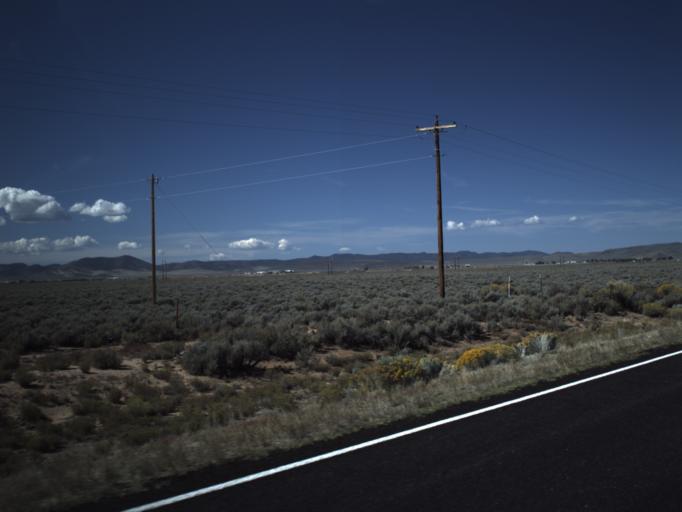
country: US
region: Utah
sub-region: Washington County
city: Enterprise
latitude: 37.6904
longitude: -113.6033
